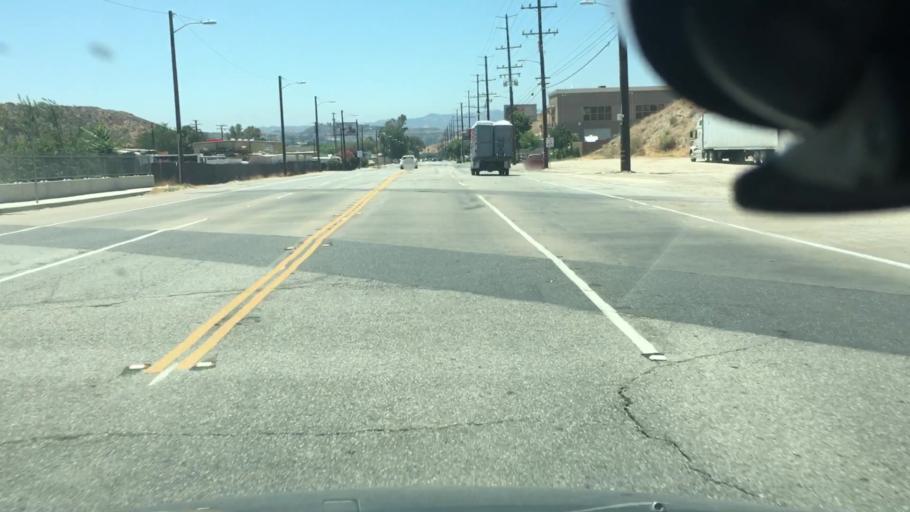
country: US
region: California
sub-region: Los Angeles County
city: Santa Clarita
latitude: 34.4306
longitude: -118.4432
